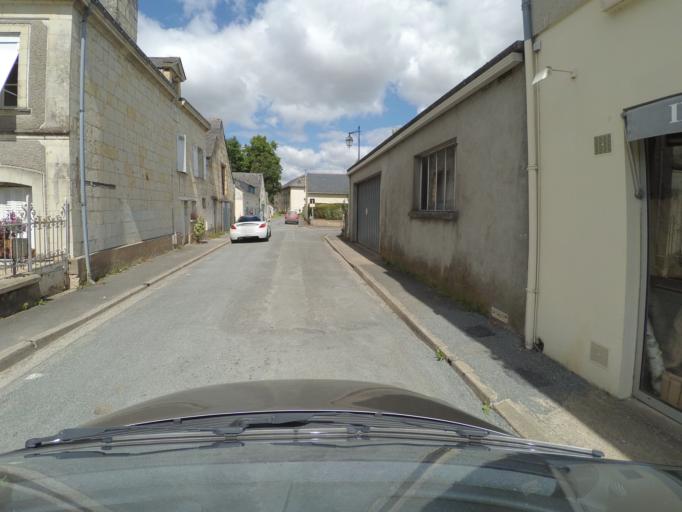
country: FR
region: Pays de la Loire
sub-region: Departement de Maine-et-Loire
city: Les Rosiers-sur-Loire
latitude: 47.3523
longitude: -0.2244
